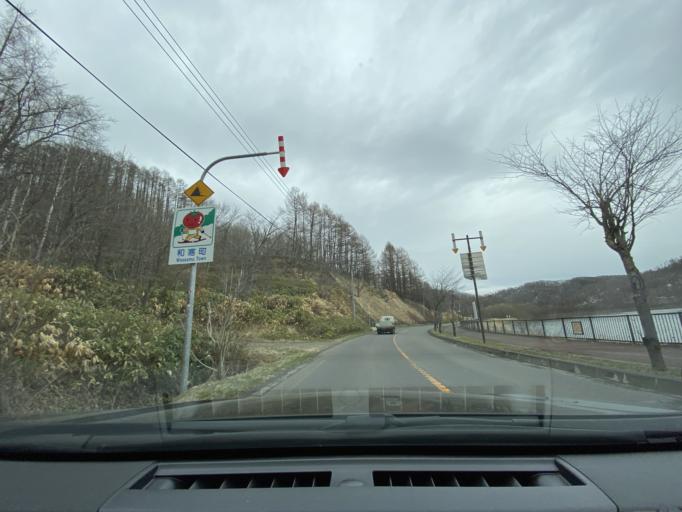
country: JP
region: Hokkaido
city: Nayoro
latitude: 44.0964
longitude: 142.4360
